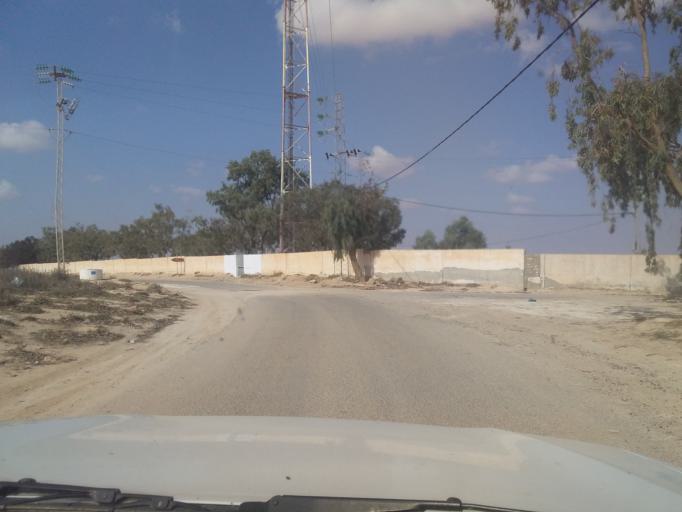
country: TN
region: Qabis
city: Gabes
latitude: 33.6312
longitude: 10.2741
